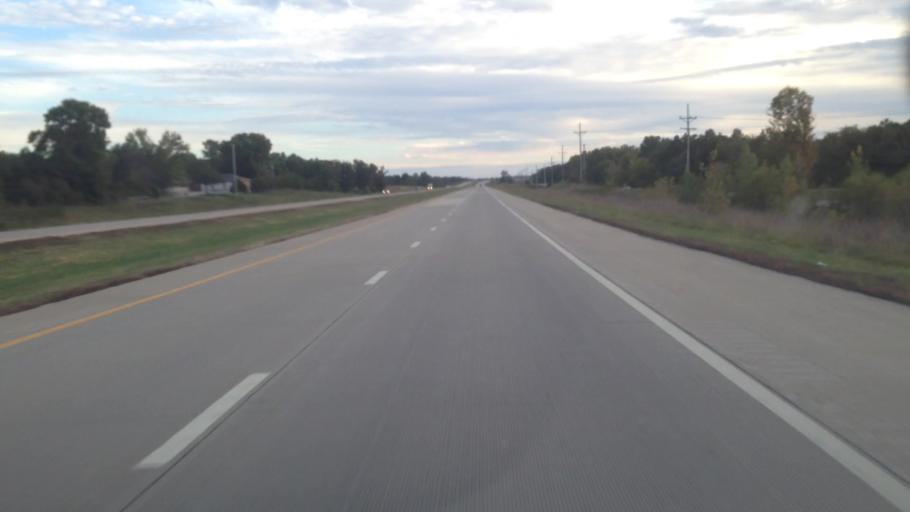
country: US
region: Kansas
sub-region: Douglas County
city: Baldwin City
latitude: 38.7551
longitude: -95.2681
